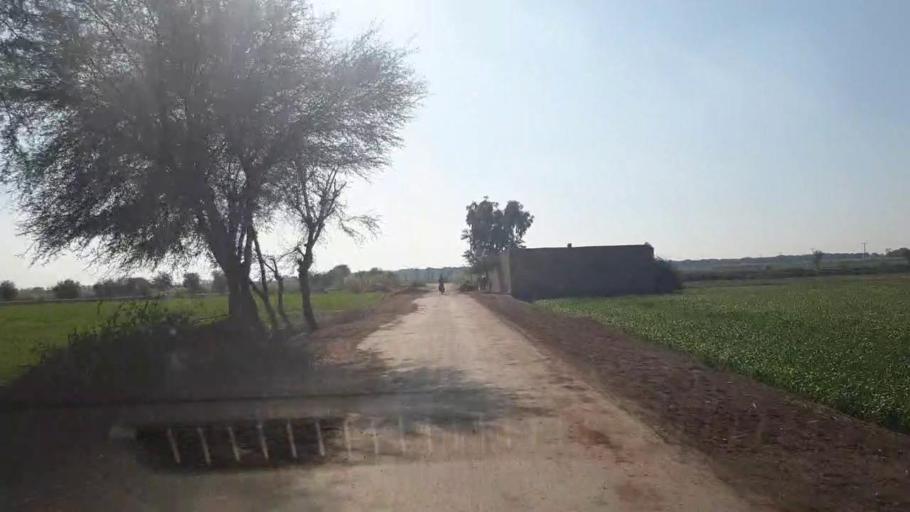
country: PK
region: Sindh
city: Shahdadpur
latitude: 25.9055
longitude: 68.5486
